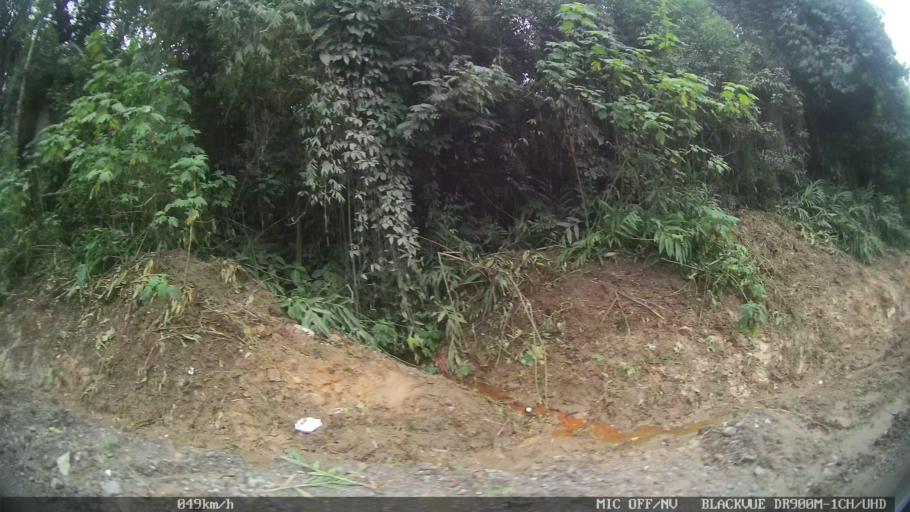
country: BR
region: Santa Catarina
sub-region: Joinville
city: Joinville
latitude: -26.2731
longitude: -48.8985
